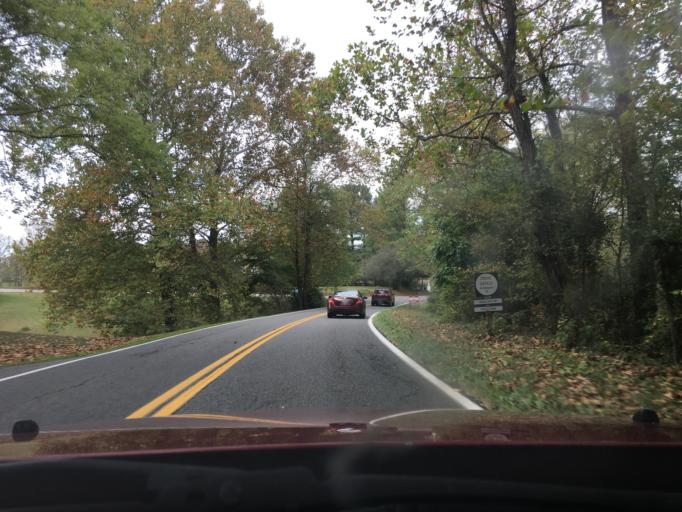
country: US
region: Virginia
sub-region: Pulaski County
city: Fairlawn
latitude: 37.1704
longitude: -80.6098
